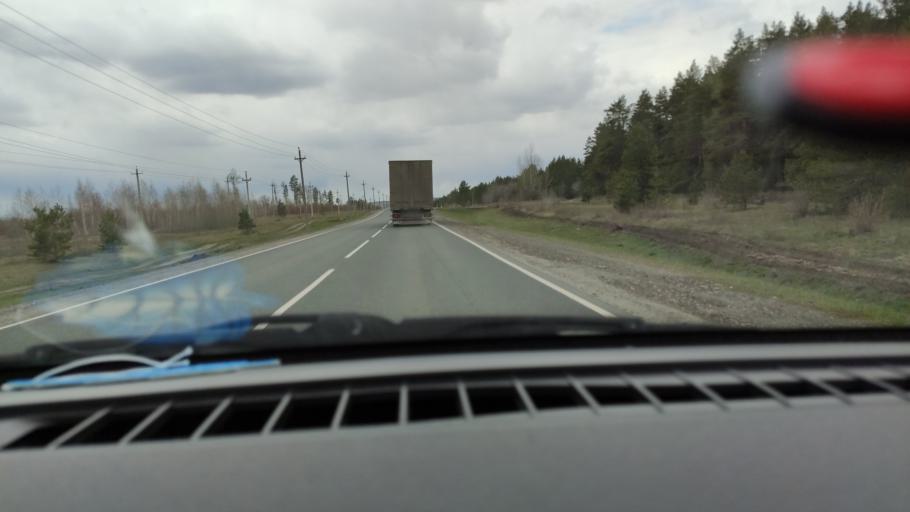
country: RU
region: Saratov
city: Sennoy
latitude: 52.1439
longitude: 46.9285
